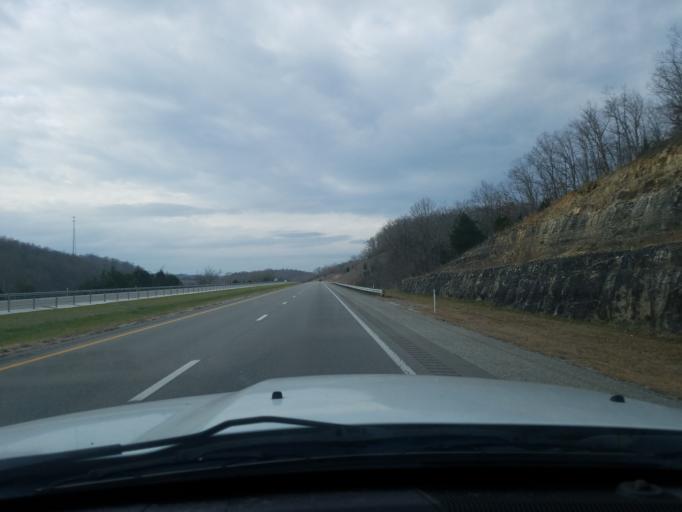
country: US
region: Kentucky
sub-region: Carter County
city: Olive Hill
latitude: 38.3296
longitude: -83.1889
